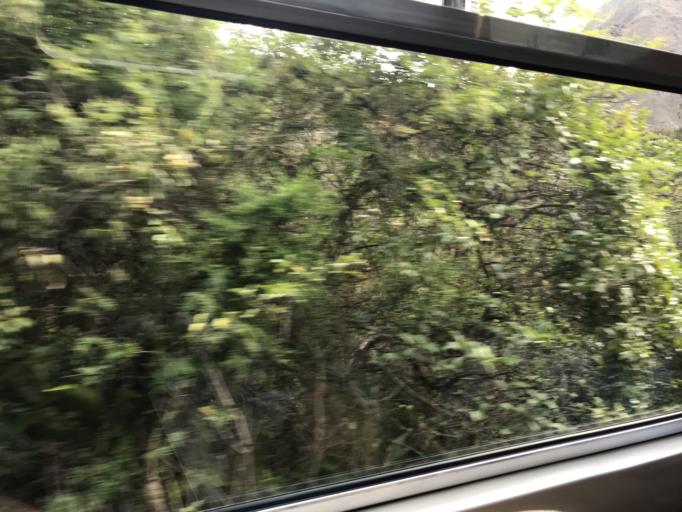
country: PE
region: Cusco
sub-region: Provincia de Urubamba
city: Ollantaytambo
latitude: -13.2259
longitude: -72.4216
